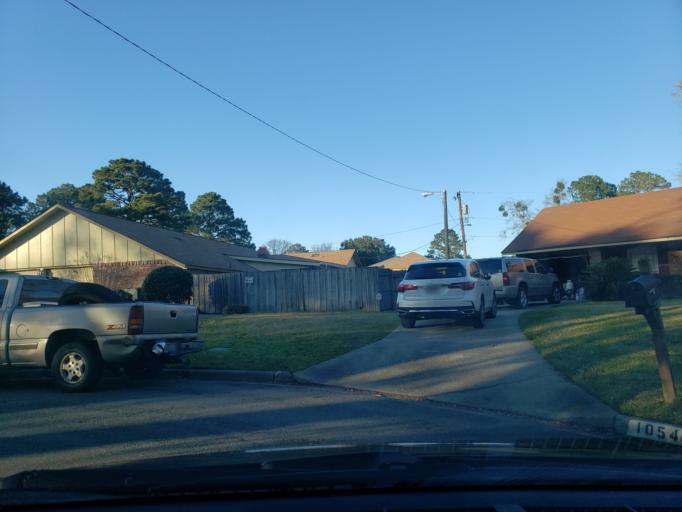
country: US
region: Georgia
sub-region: Chatham County
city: Montgomery
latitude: 31.9980
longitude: -81.1440
